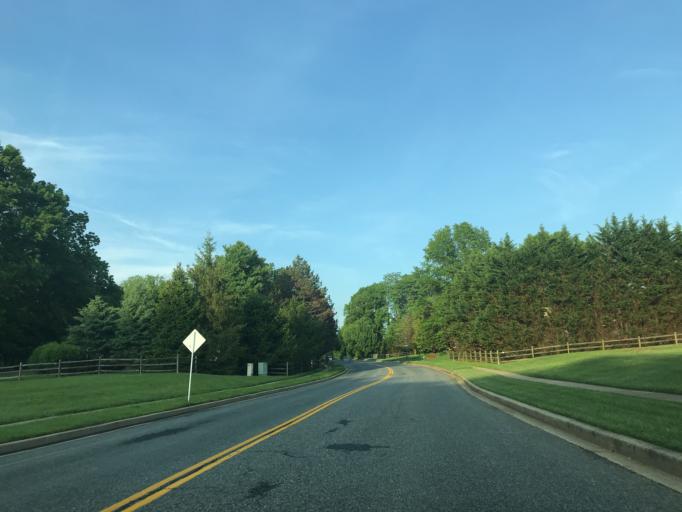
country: US
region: Maryland
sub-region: Harford County
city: North Bel Air
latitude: 39.5568
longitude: -76.3429
